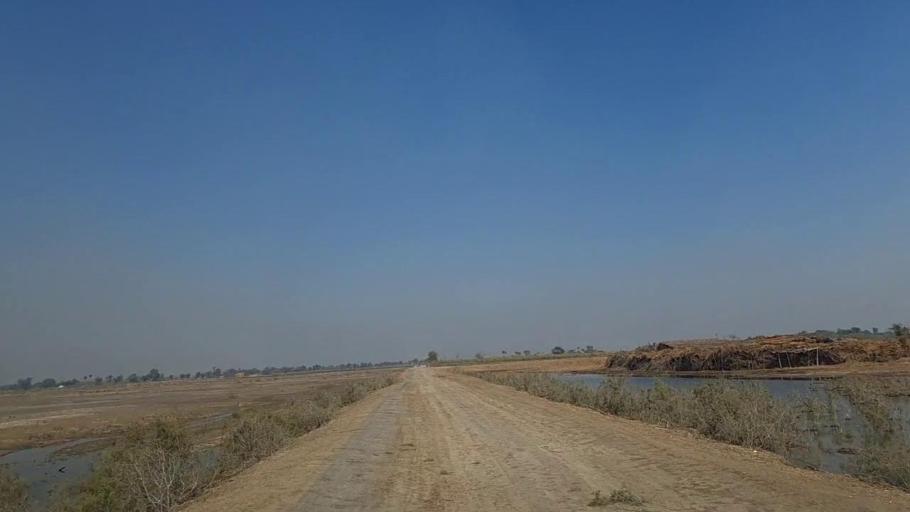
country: PK
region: Sindh
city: Daur
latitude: 26.4762
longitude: 68.3253
